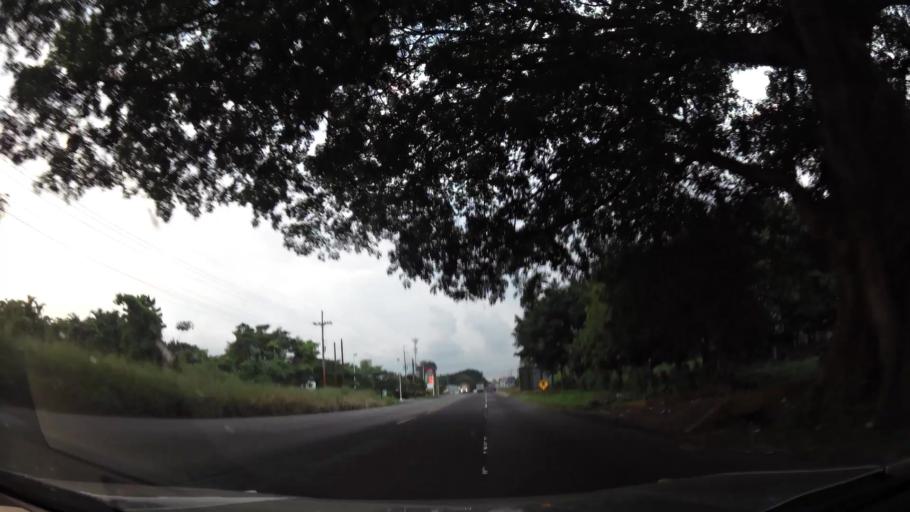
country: GT
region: Escuintla
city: Siquinala
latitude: 14.2867
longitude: -90.9378
